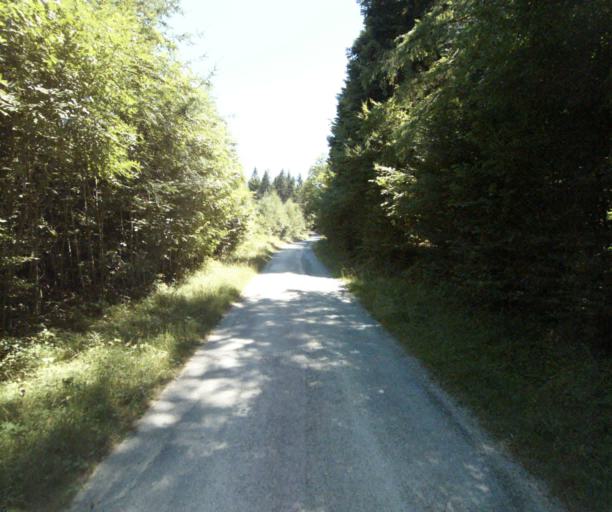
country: FR
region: Languedoc-Roussillon
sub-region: Departement de l'Aude
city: Cuxac-Cabardes
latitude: 43.4029
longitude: 2.2089
